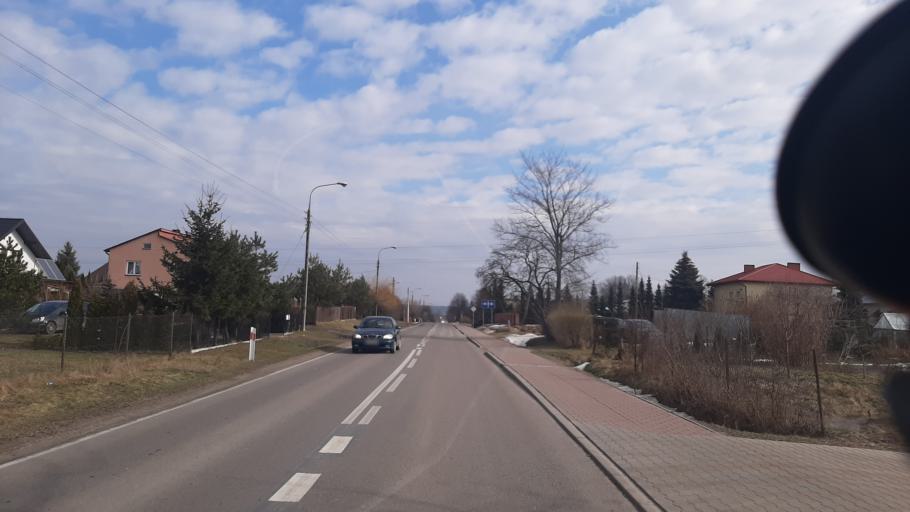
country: PL
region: Lublin Voivodeship
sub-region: Powiat lubelski
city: Niemce
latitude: 51.3587
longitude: 22.6065
